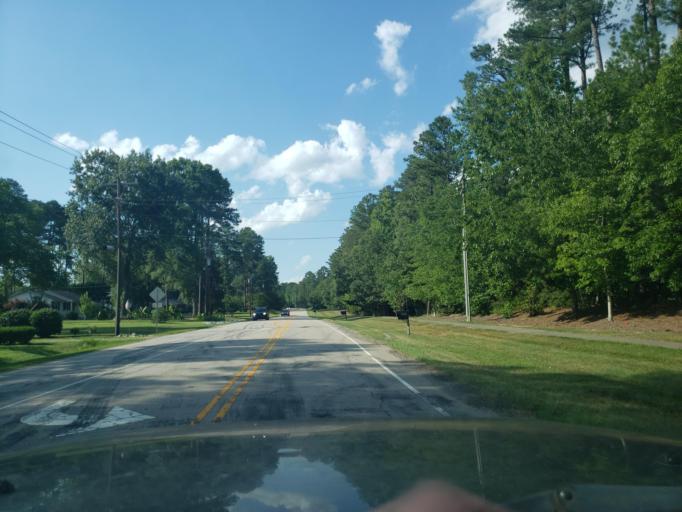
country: US
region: North Carolina
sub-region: Durham County
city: Durham
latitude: 35.9786
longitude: -78.9901
